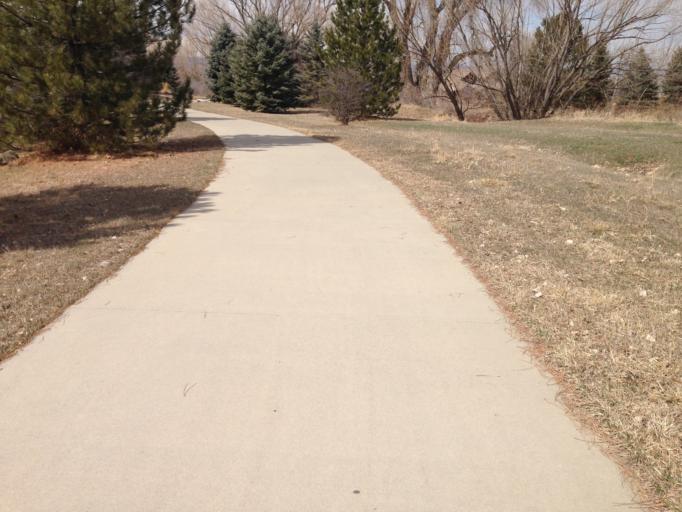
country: US
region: Colorado
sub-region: Boulder County
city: Louisville
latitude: 40.0085
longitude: -105.1414
